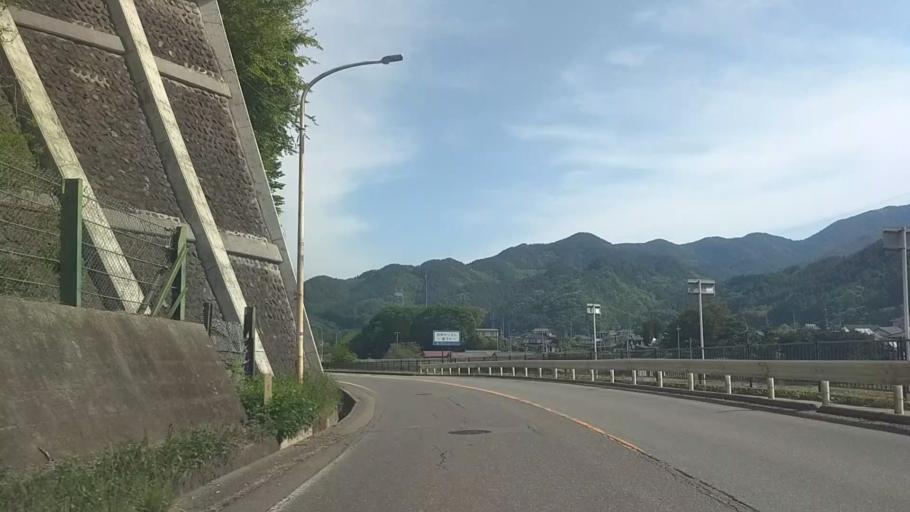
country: JP
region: Nagano
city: Saku
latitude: 36.0984
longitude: 138.4824
